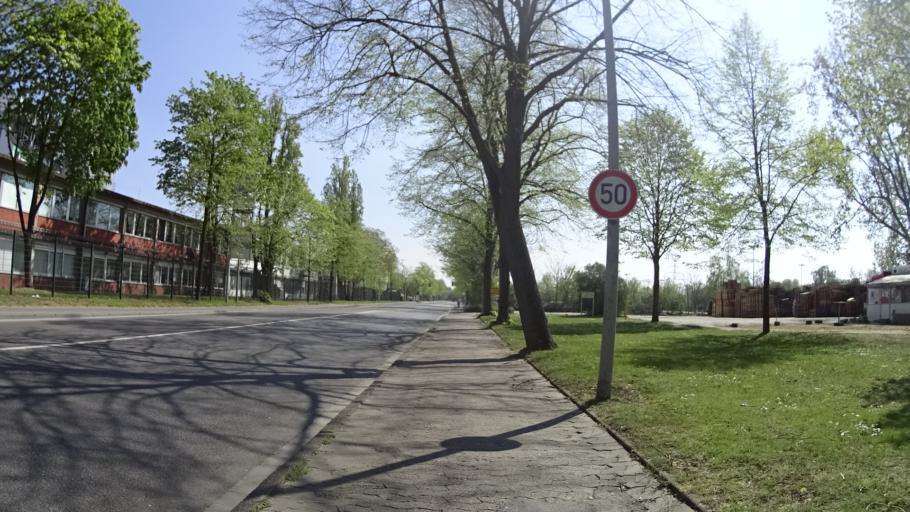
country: DE
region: North Rhine-Westphalia
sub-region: Regierungsbezirk Dusseldorf
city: Krefeld
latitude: 51.3401
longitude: 6.6616
